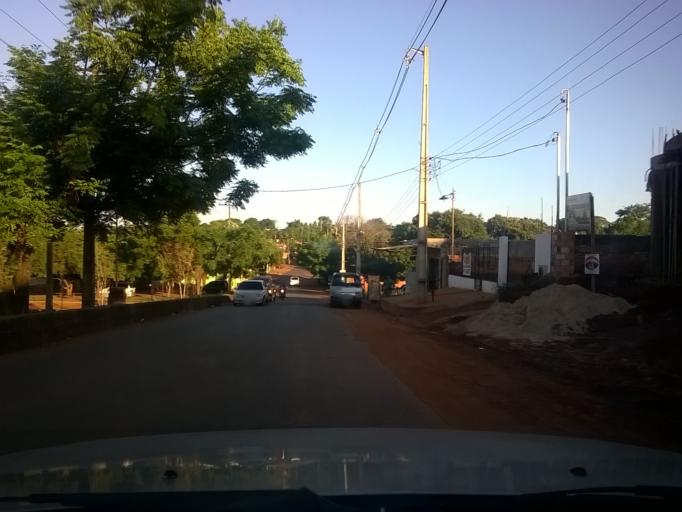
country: PY
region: Alto Parana
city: Presidente Franco
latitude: -25.5340
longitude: -54.6464
